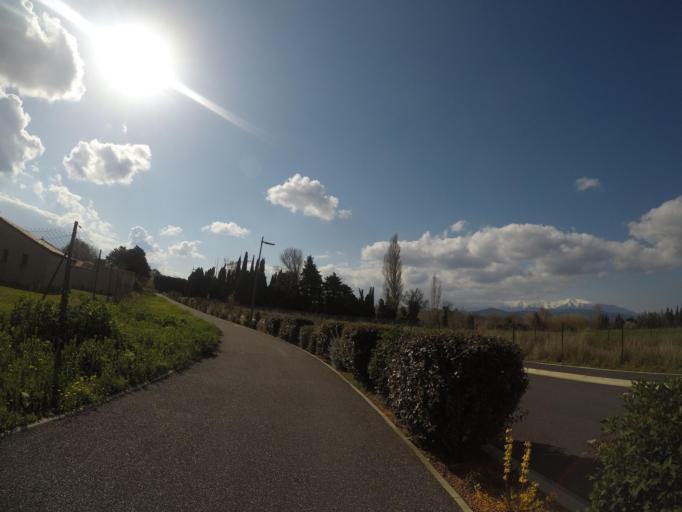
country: FR
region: Languedoc-Roussillon
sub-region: Departement des Pyrenees-Orientales
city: Millas
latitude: 42.6854
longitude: 2.6876
